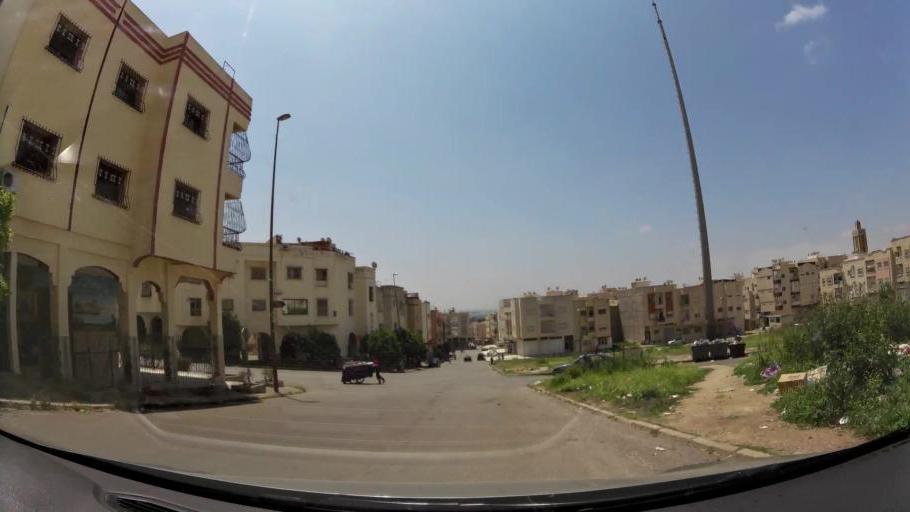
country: MA
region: Fes-Boulemane
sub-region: Fes
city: Fes
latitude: 34.0623
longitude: -5.0206
